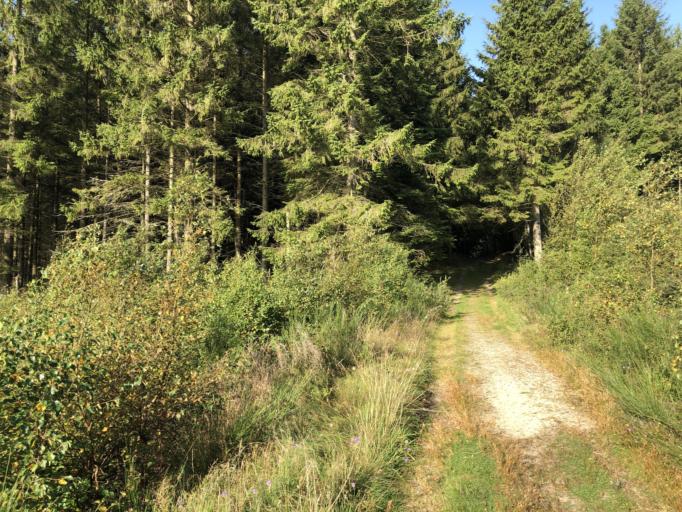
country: DK
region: Central Jutland
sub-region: Lemvig Kommune
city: Lemvig
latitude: 56.4732
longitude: 8.3327
